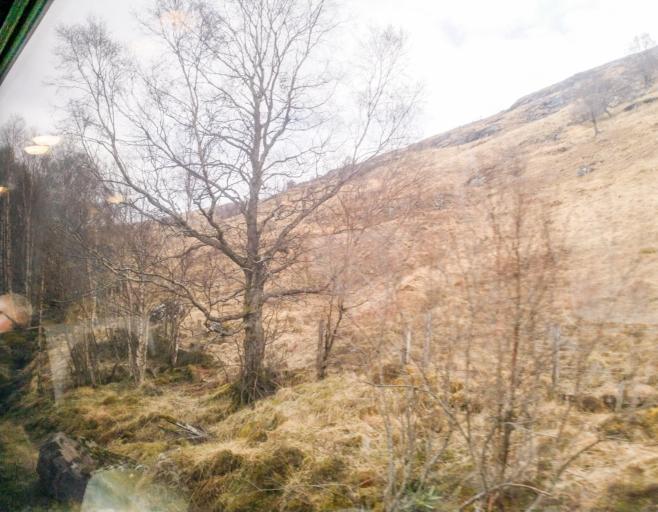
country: GB
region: Scotland
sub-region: Highland
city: Spean Bridge
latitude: 56.7915
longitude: -4.7268
